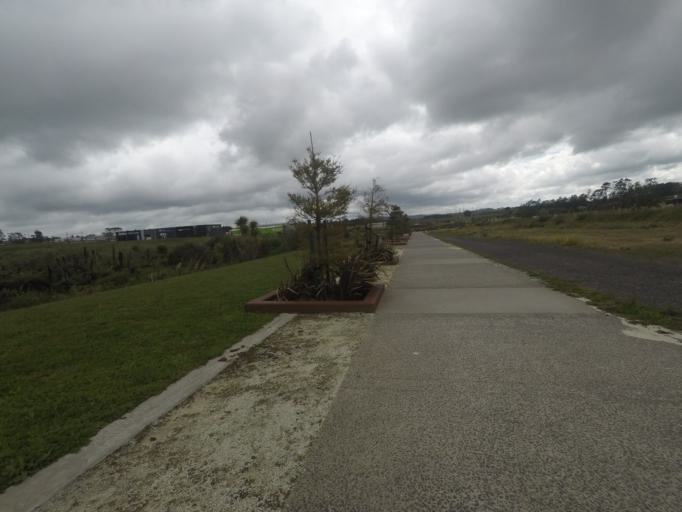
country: NZ
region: Auckland
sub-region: Auckland
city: Rosebank
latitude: -36.8139
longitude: 174.6069
